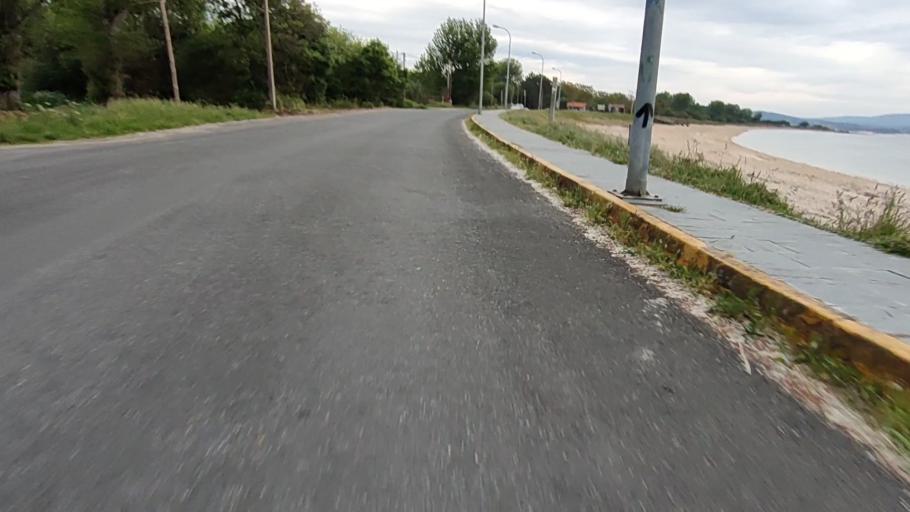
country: ES
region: Galicia
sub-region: Provincia da Coruna
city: Boiro
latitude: 42.6141
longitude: -8.8766
